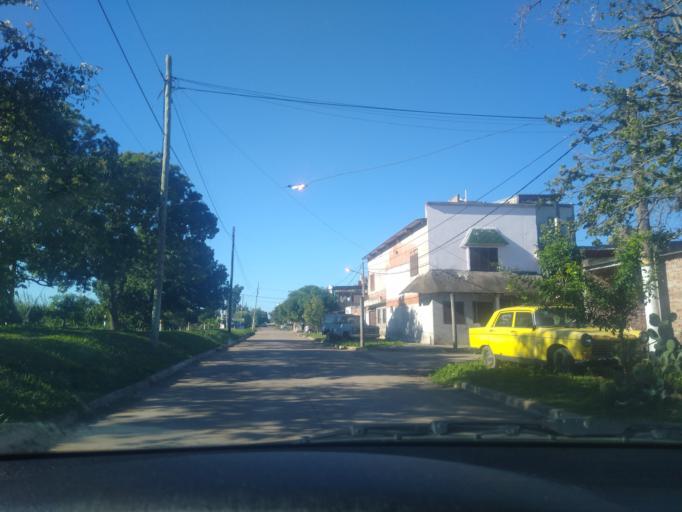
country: AR
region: Chaco
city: Puerto Vilelas
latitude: -27.5165
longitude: -58.9451
